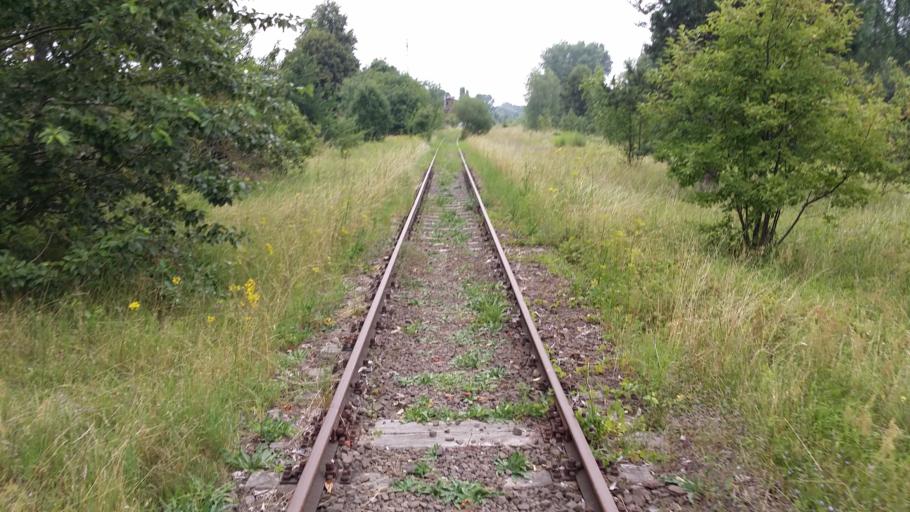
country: PL
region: West Pomeranian Voivodeship
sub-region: Powiat choszczenski
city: Drawno
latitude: 53.2128
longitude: 15.7674
